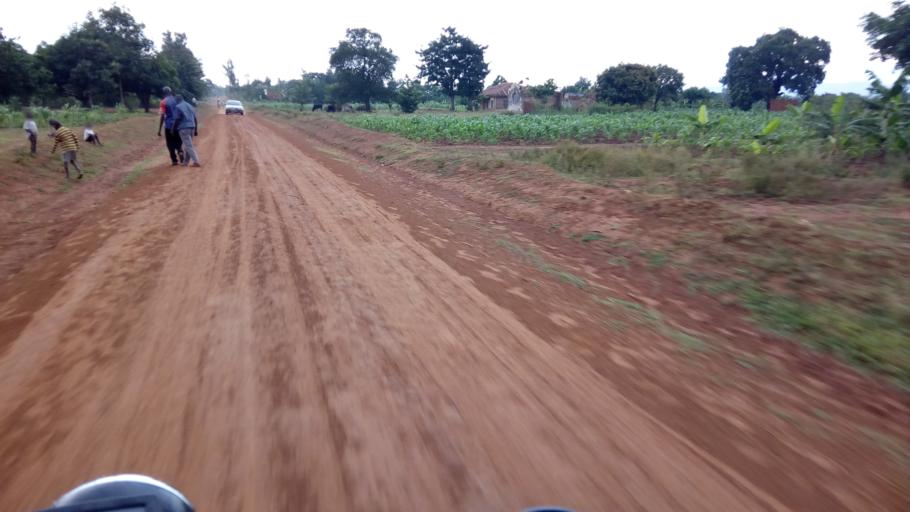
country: UG
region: Eastern Region
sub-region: Mbale District
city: Mbale
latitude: 1.1277
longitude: 34.1043
